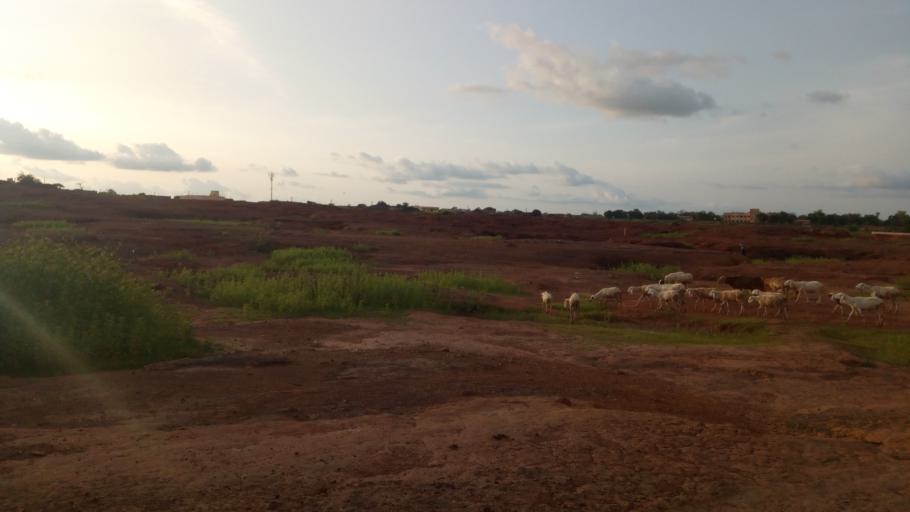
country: ML
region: Sikasso
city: Koutiala
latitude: 12.3719
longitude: -5.4775
